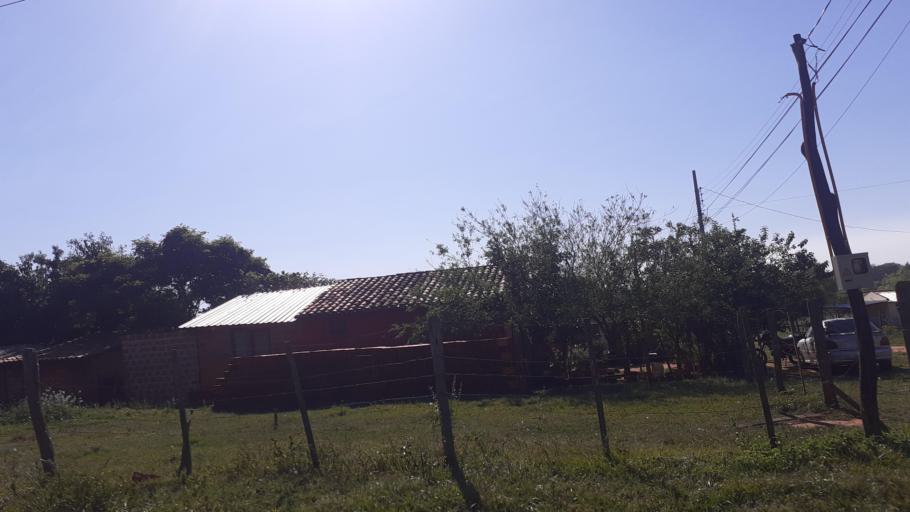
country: PY
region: Misiones
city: San Juan Bautista
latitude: -26.6649
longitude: -57.1245
